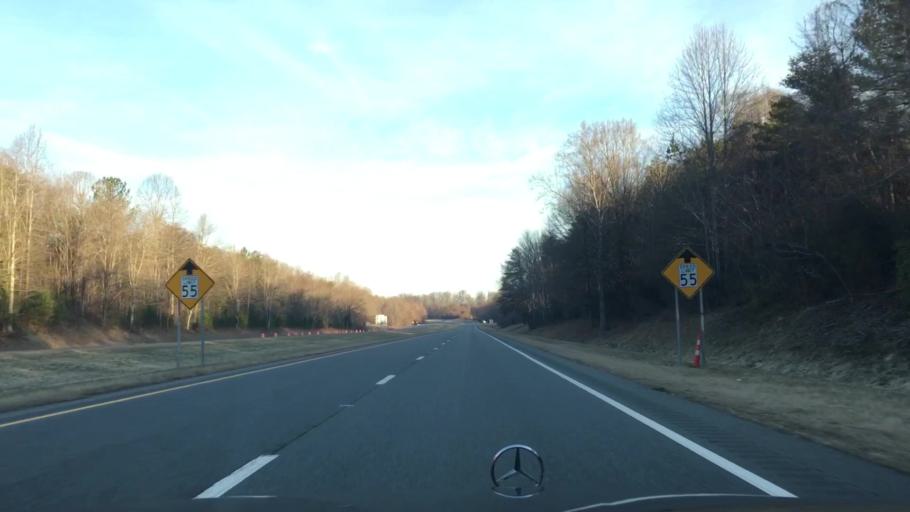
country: US
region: North Carolina
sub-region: Guilford County
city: Pleasant Garden
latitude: 36.0145
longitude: -79.7609
